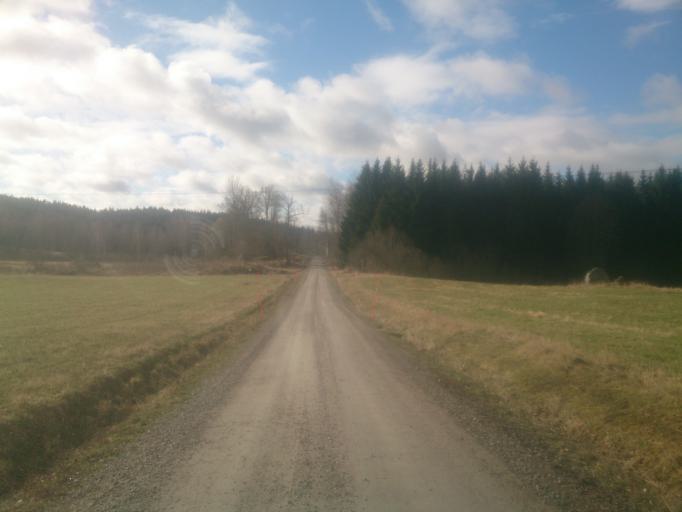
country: SE
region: OEstergoetland
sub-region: Atvidabergs Kommun
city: Atvidaberg
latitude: 58.2330
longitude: 16.1784
